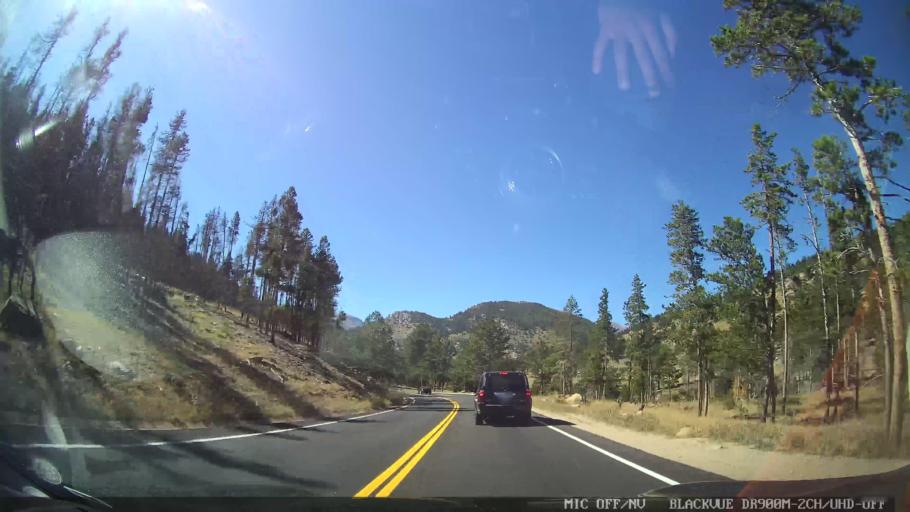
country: US
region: Colorado
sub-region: Larimer County
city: Estes Park
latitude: 40.3417
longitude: -105.5966
